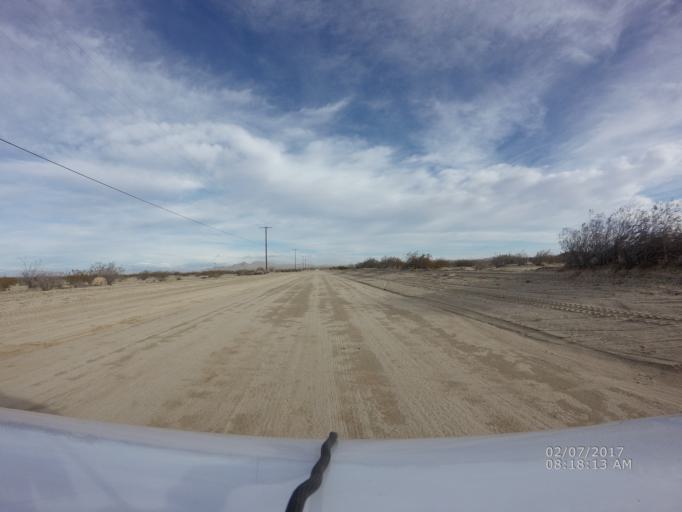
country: US
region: California
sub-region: Los Angeles County
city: Lake Los Angeles
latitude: 34.5850
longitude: -117.7736
